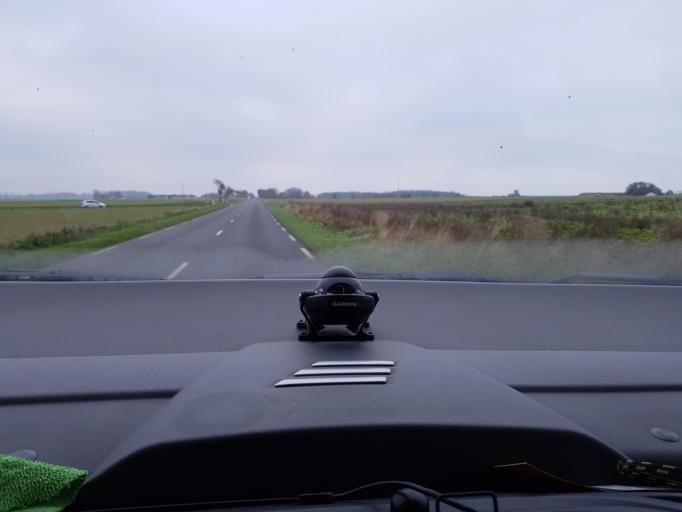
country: FR
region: Picardie
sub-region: Departement de la Somme
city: Ault
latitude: 50.1016
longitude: 1.4705
